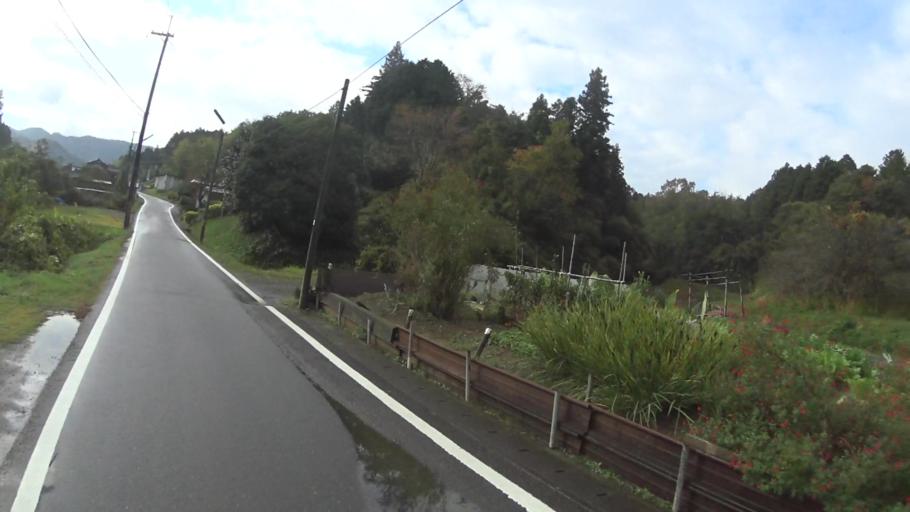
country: JP
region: Kyoto
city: Ayabe
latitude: 35.2879
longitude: 135.2380
